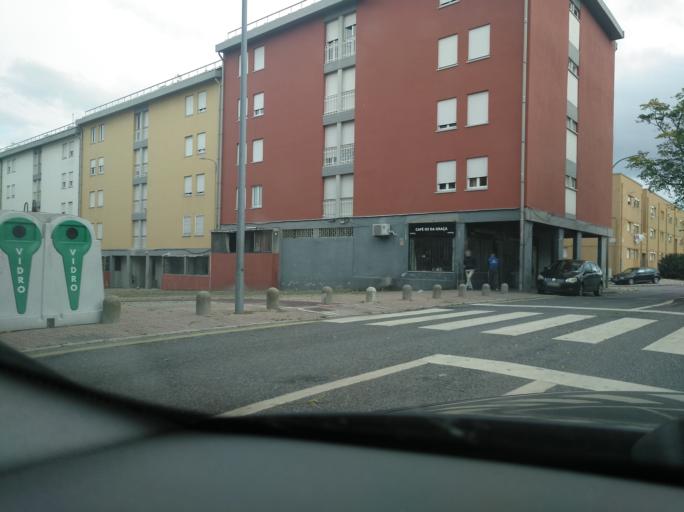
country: PT
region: Lisbon
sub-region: Amadora
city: Amadora
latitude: 38.7386
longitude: -9.2098
